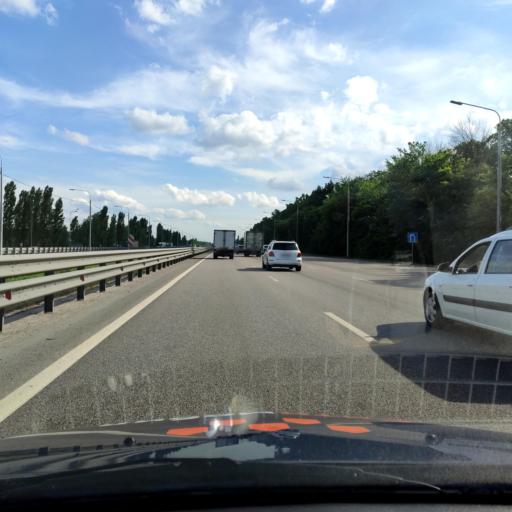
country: RU
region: Voronezj
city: Podgornoye
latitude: 51.7831
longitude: 39.1955
